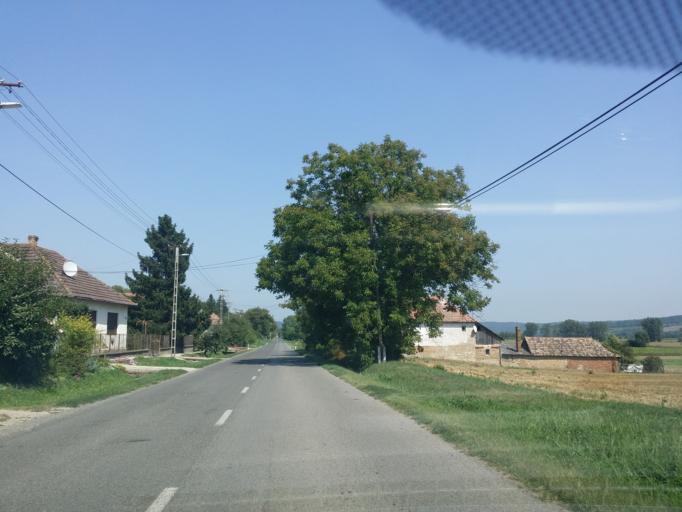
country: HU
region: Tolna
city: Hogyesz
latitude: 46.5724
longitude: 18.3812
